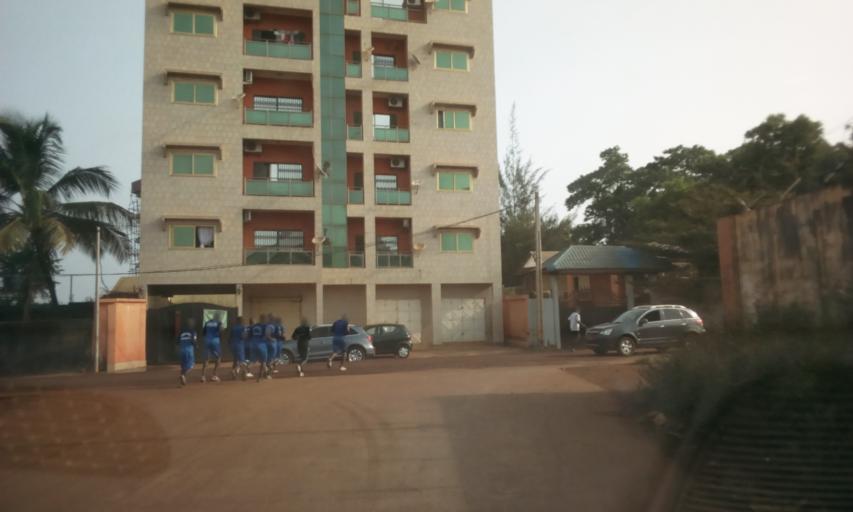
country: GN
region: Conakry
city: Conakry
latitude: 9.6276
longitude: -13.6272
